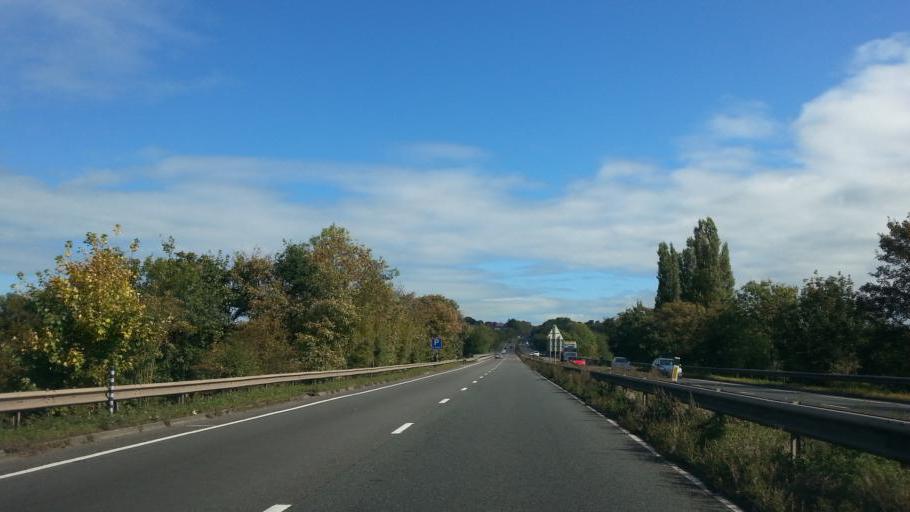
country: GB
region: England
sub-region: Herefordshire
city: Ross on Wye
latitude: 51.9182
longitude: -2.5963
